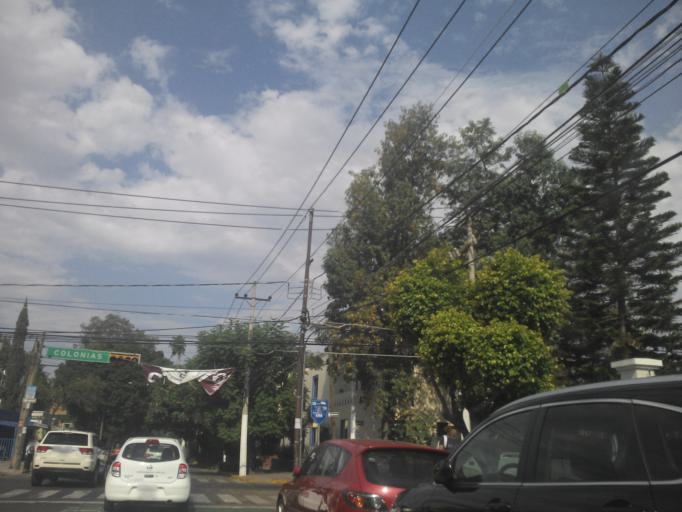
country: MX
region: Jalisco
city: Guadalajara
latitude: 20.6738
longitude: -103.3664
